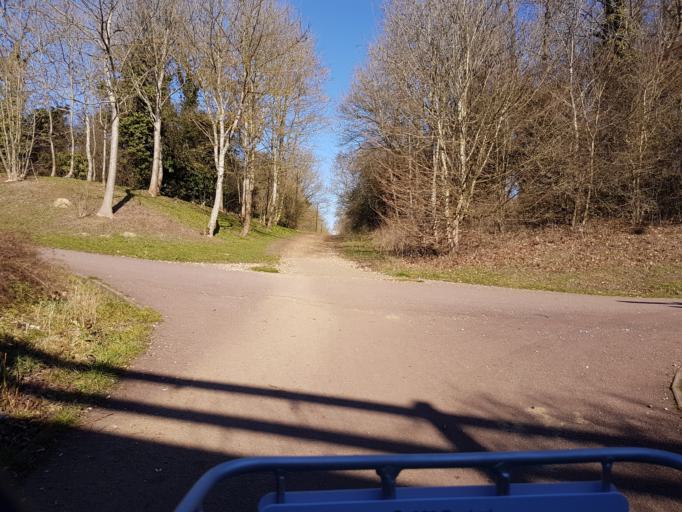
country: GB
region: England
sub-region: Milton Keynes
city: Milton Keynes
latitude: 52.0207
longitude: -0.7518
